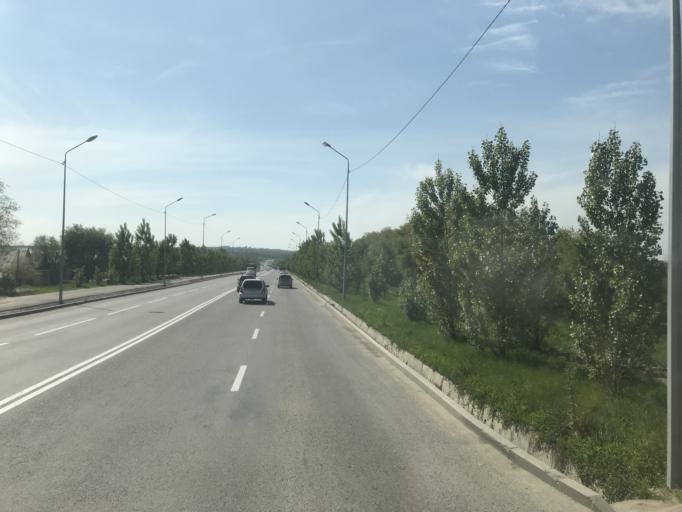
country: KZ
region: Almaty Oblysy
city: Burunday
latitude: 43.3122
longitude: 76.8596
